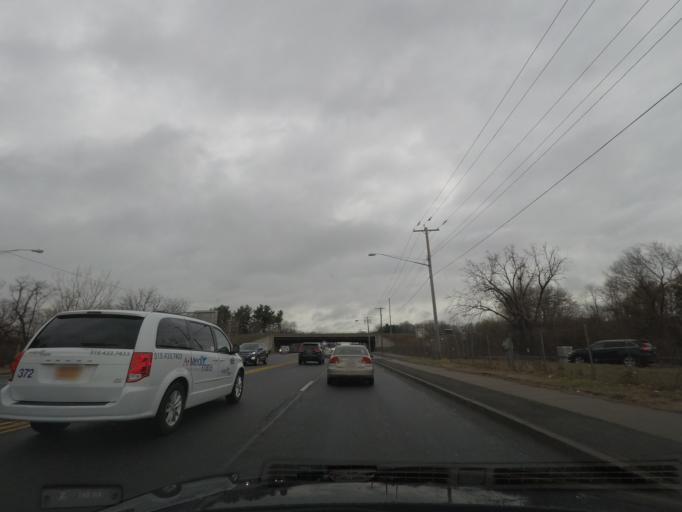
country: US
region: New York
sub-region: Albany County
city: Colonie
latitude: 42.7096
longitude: -73.8236
